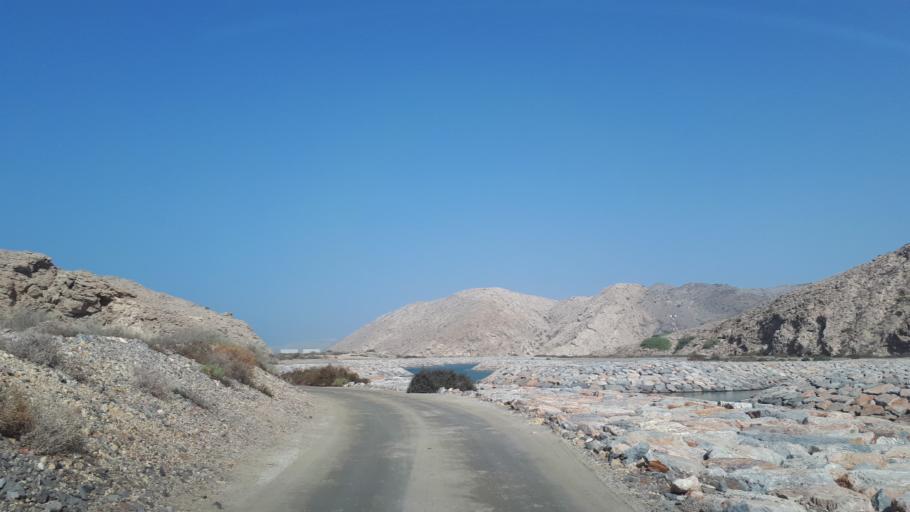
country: OM
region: Muhafazat Masqat
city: Muscat
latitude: 23.5391
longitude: 58.6605
